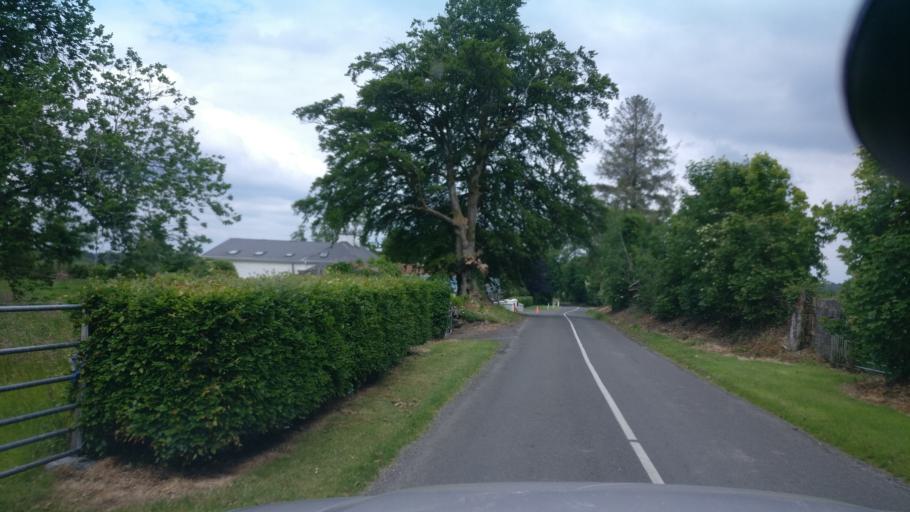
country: IE
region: Connaught
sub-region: County Galway
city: Ballinasloe
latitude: 53.2640
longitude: -8.3601
